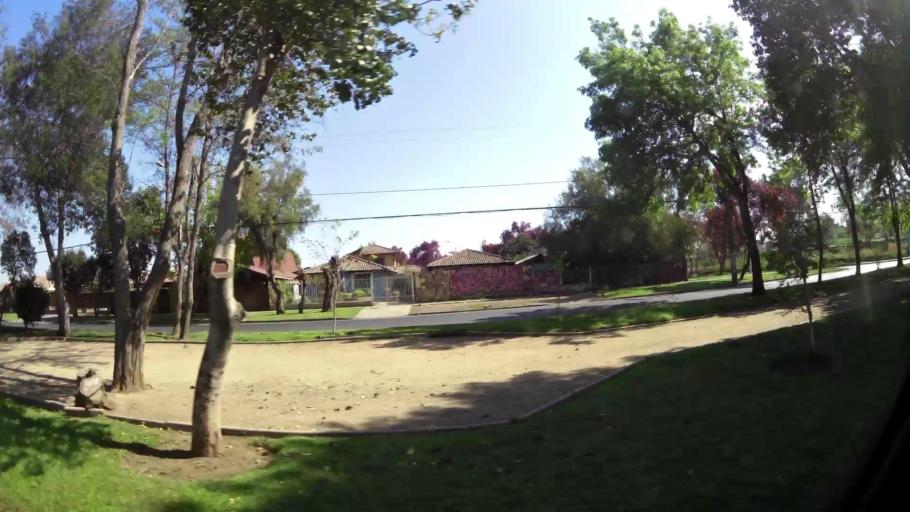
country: CL
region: Santiago Metropolitan
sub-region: Provincia de Santiago
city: Lo Prado
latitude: -33.4719
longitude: -70.7276
